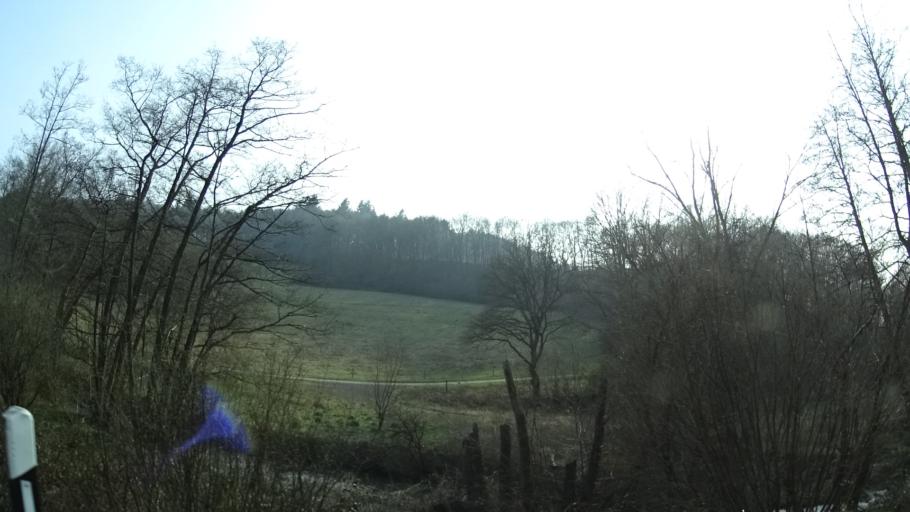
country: DE
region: Rheinland-Pfalz
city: Altenglan
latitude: 49.5508
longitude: 7.4792
